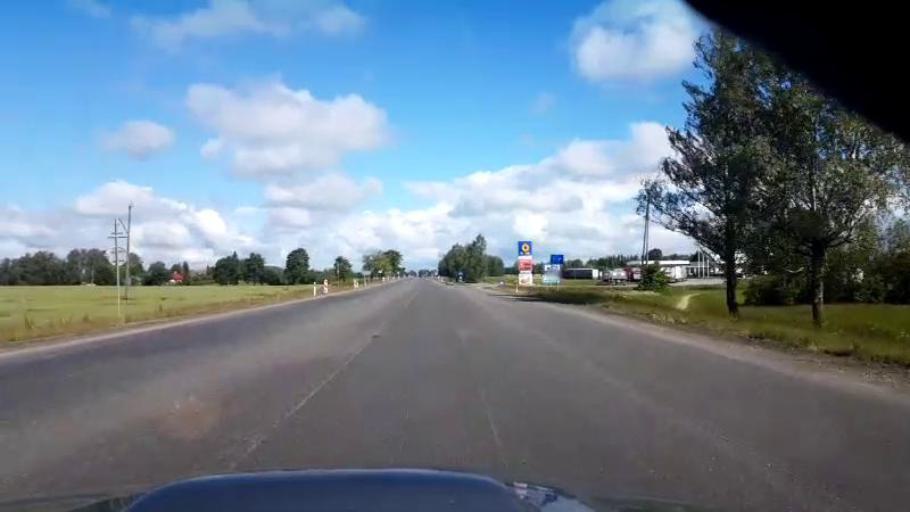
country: LV
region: Bauskas Rajons
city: Bauska
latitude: 56.3653
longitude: 24.2783
